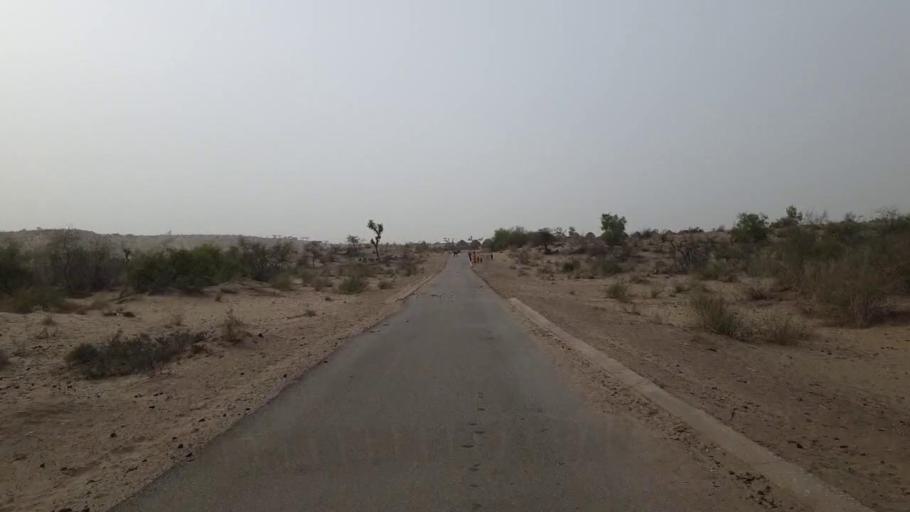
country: PK
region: Sindh
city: Islamkot
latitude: 24.5763
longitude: 70.3656
